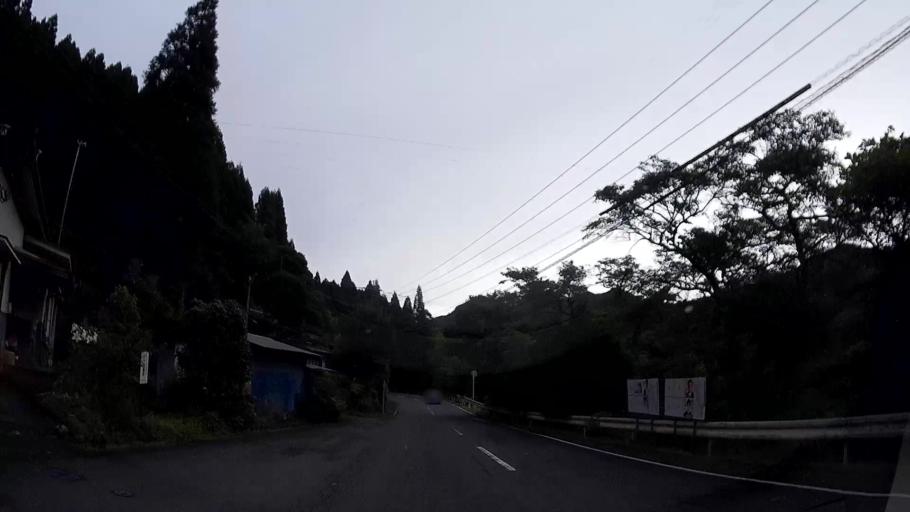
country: JP
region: Kumamoto
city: Kikuchi
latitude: 33.0936
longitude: 130.9558
